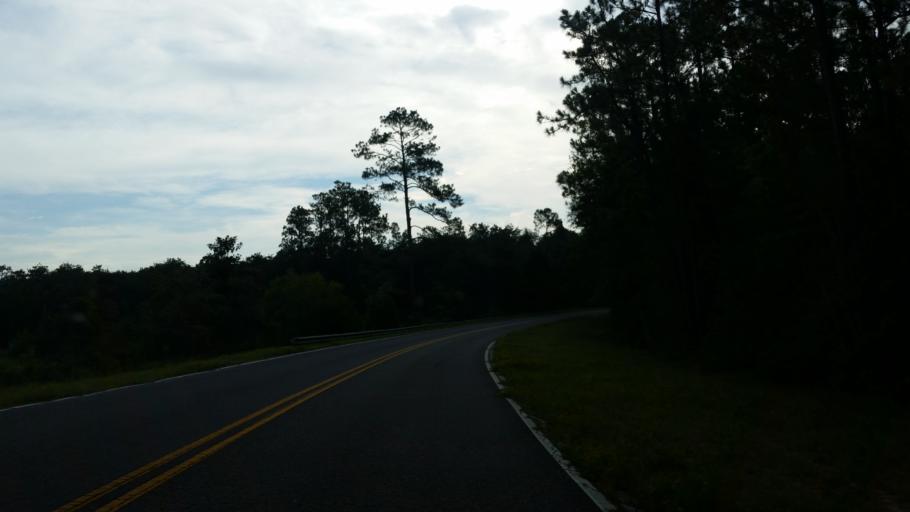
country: US
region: Florida
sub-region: Escambia County
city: Molino
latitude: 30.7740
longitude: -87.4953
